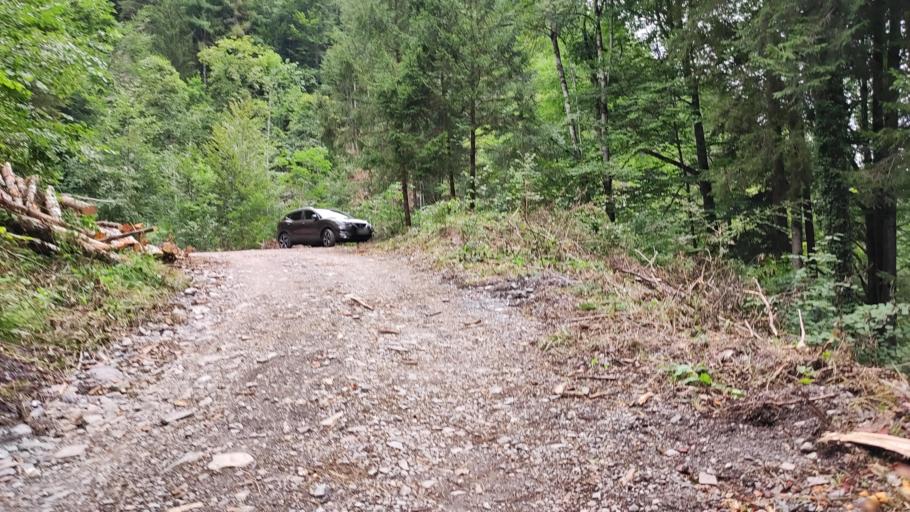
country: AT
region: Vorarlberg
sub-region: Politischer Bezirk Feldkirch
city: Feldkirch
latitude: 47.1997
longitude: 9.6062
